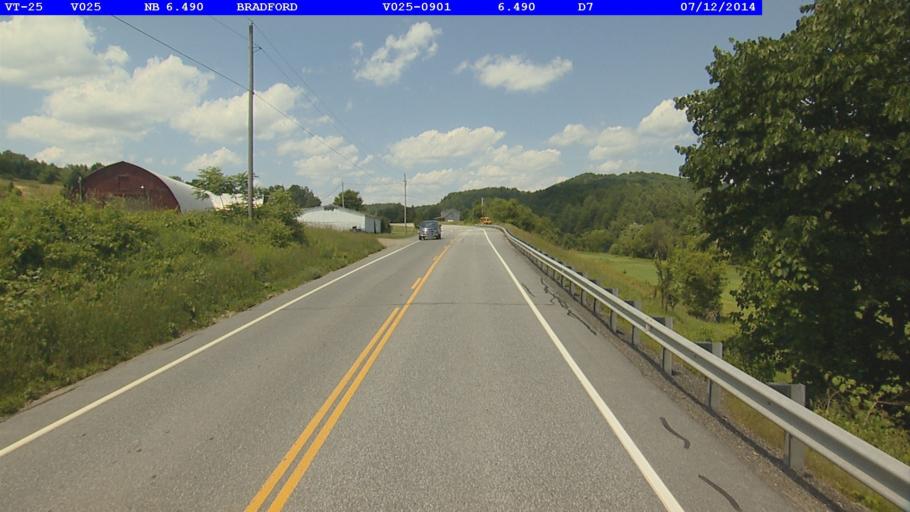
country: US
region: New Hampshire
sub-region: Grafton County
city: Haverhill
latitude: 44.0358
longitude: -72.1969
